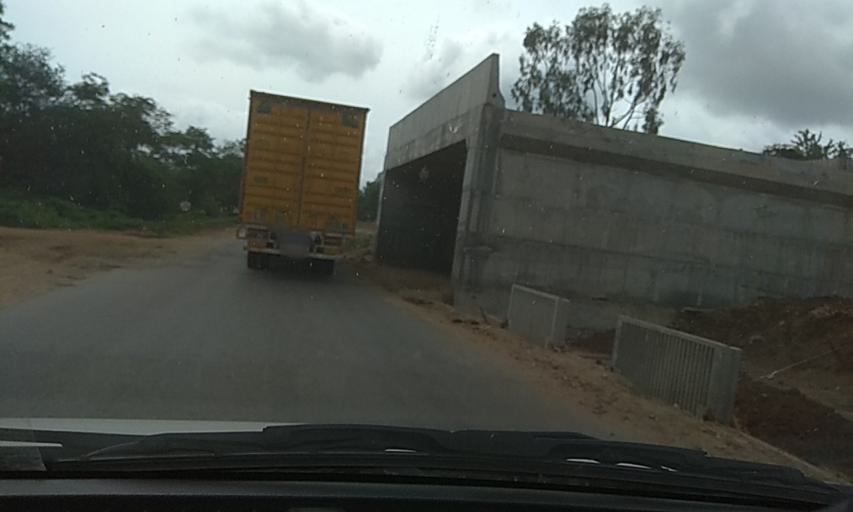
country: IN
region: Karnataka
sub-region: Davanagere
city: Mayakonda
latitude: 14.3888
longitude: 76.0614
